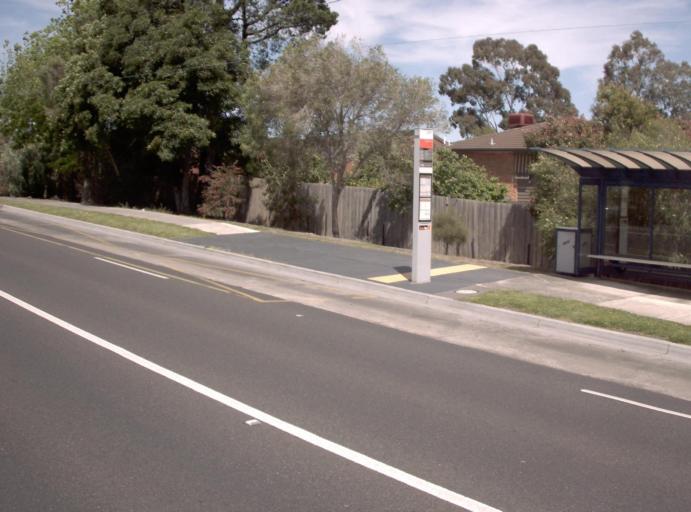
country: AU
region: Victoria
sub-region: Manningham
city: Donvale
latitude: -37.7720
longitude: 145.1651
